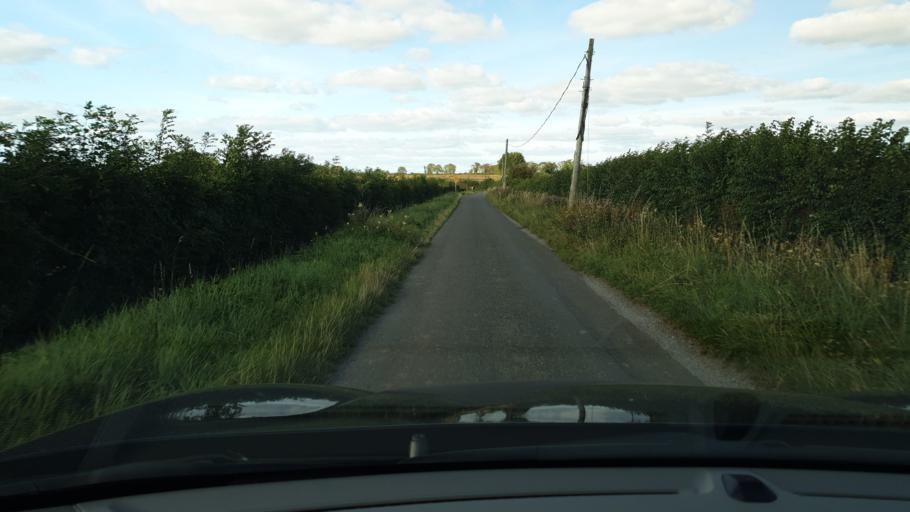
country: IE
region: Leinster
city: Hartstown
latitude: 53.4410
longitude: -6.4293
